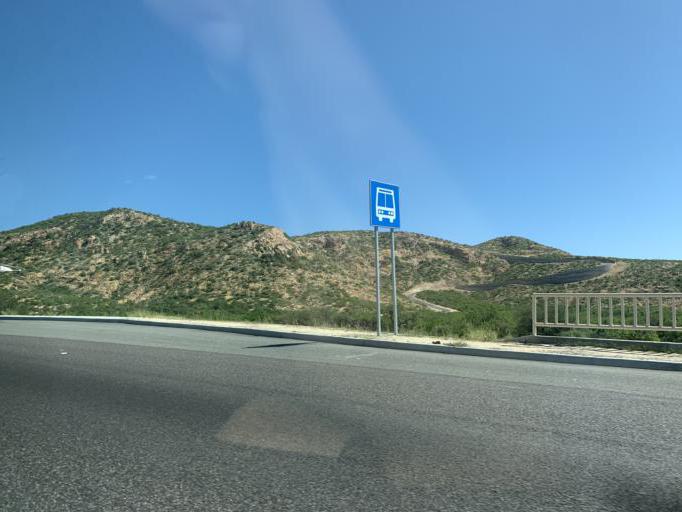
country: MX
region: Baja California Sur
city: Cabo San Lucas
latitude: 22.9365
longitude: -109.8162
